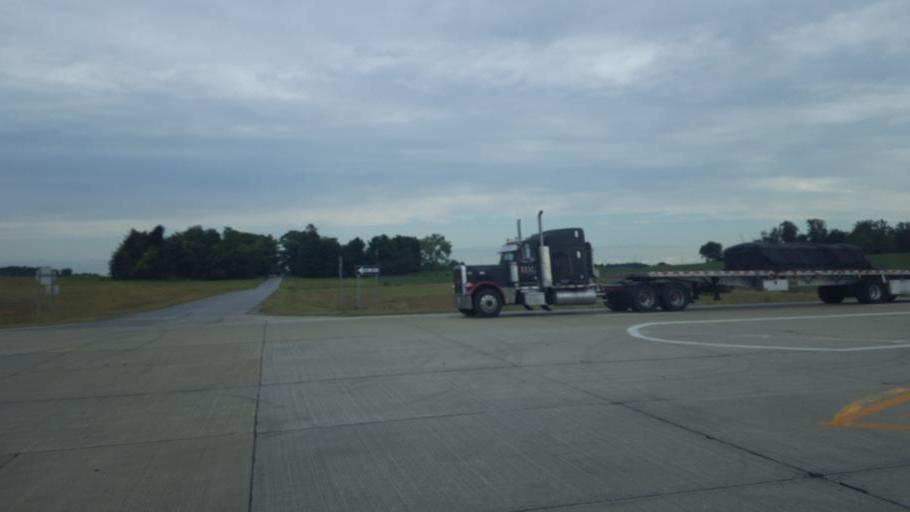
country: US
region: Ohio
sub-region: Wyandot County
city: Upper Sandusky
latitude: 40.8076
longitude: -83.1886
